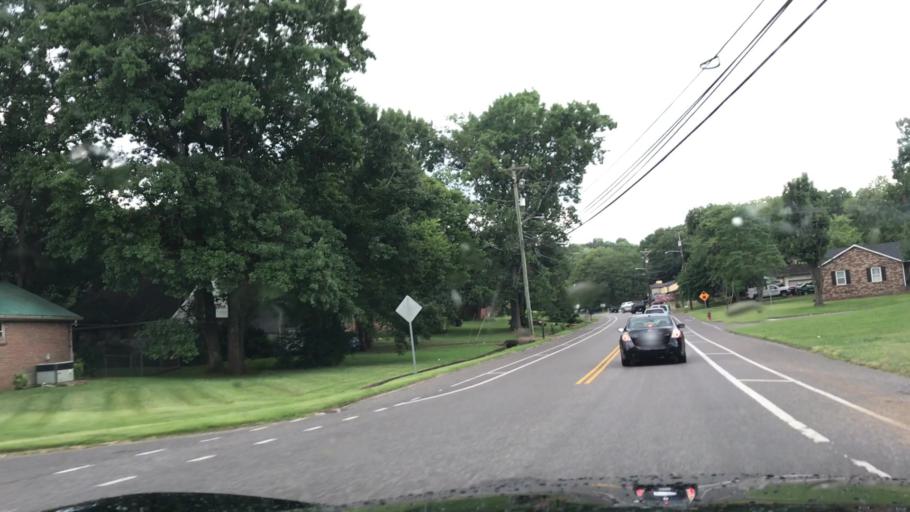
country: US
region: Tennessee
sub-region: Williamson County
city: Brentwood Estates
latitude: 36.0414
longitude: -86.7037
